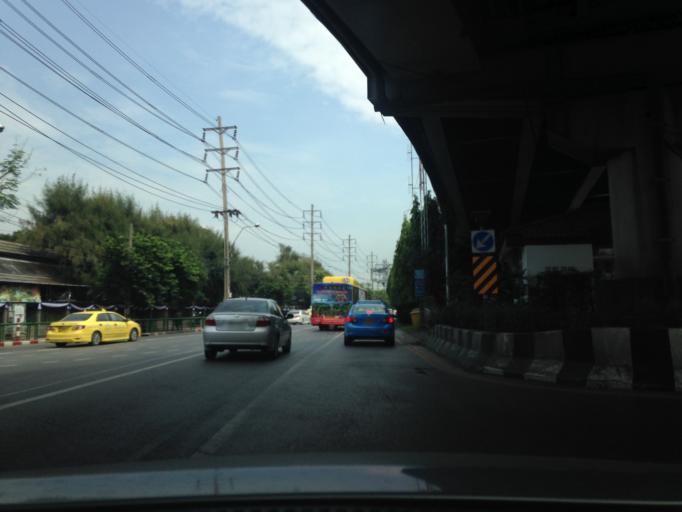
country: TH
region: Bangkok
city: Bang Sue
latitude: 13.7979
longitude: 100.5510
